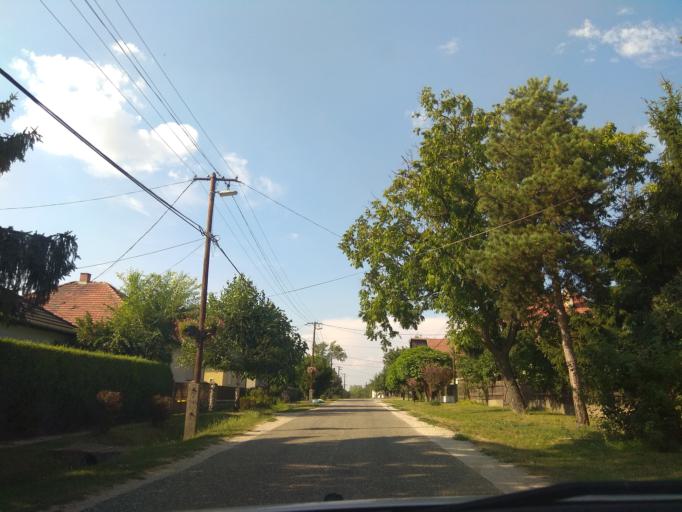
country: HU
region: Borsod-Abauj-Zemplen
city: Emod
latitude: 47.9350
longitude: 20.8152
